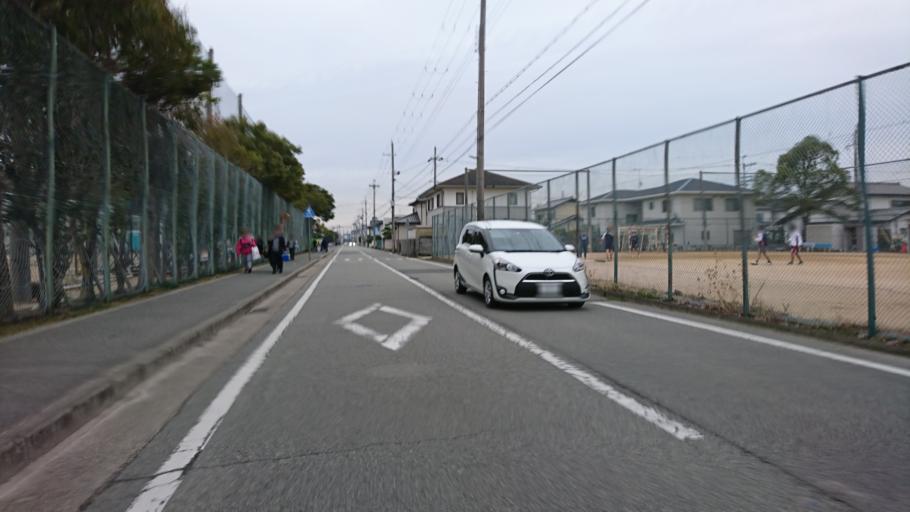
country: JP
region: Hyogo
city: Kakogawacho-honmachi
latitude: 34.7680
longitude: 134.8176
